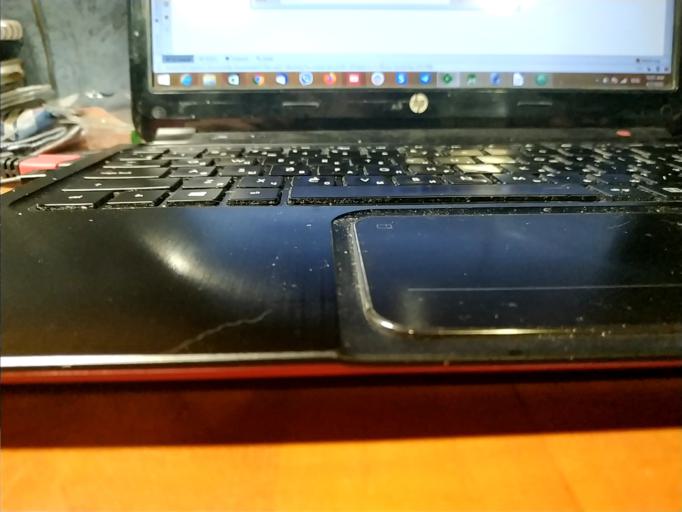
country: RU
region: Vologda
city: Suda
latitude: 58.9153
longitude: 37.5432
